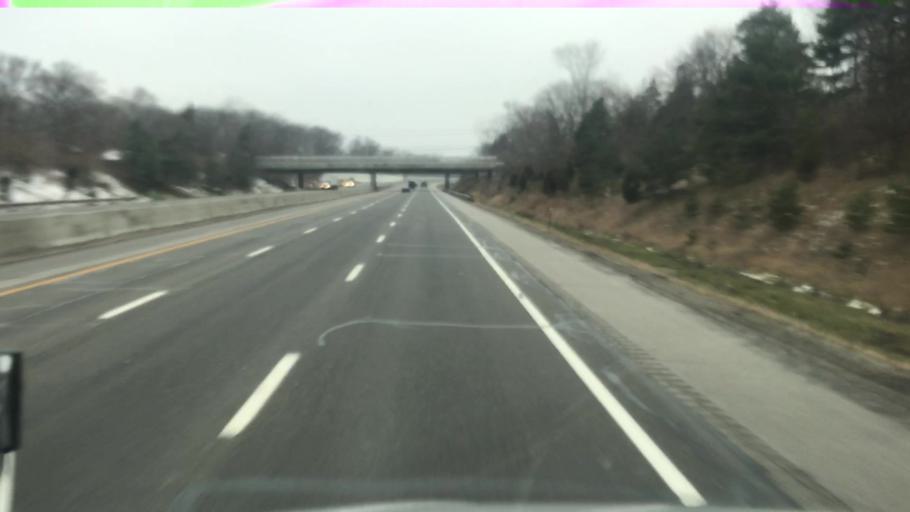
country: US
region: Ohio
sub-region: Cuyahoga County
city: Olmsted Falls
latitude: 41.3573
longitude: -81.9014
